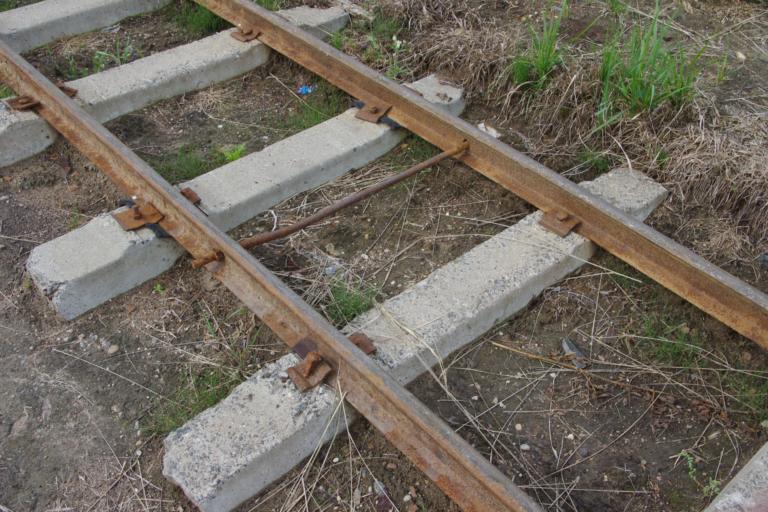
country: BY
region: Vitebsk
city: Chashniki
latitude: 55.3399
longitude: 29.3094
